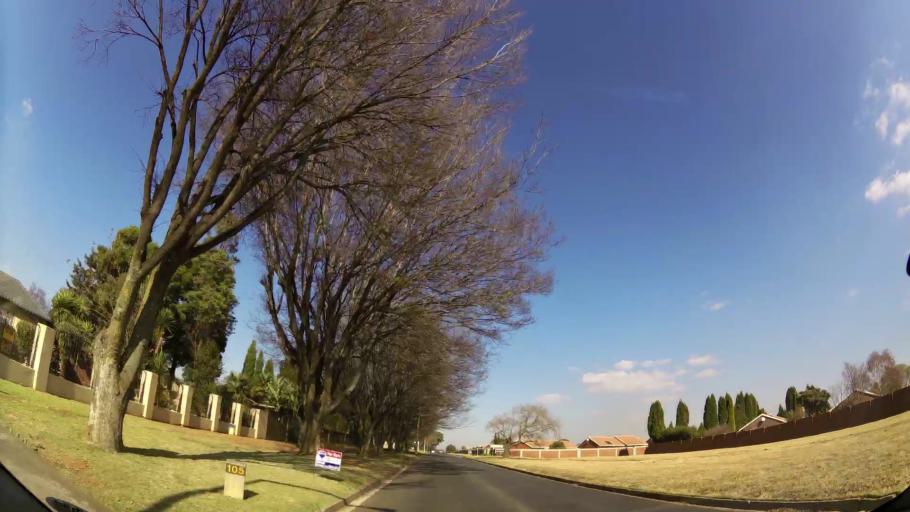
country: ZA
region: Gauteng
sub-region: Ekurhuleni Metropolitan Municipality
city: Benoni
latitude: -26.1381
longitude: 28.3402
